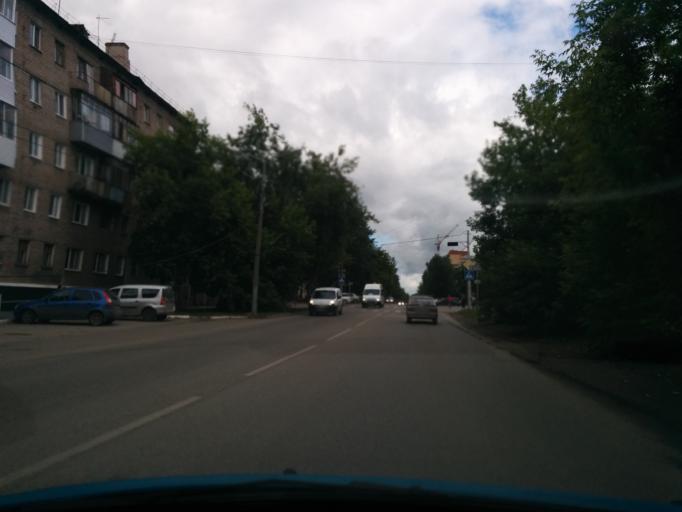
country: RU
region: Perm
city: Kondratovo
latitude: 58.0254
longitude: 56.0149
